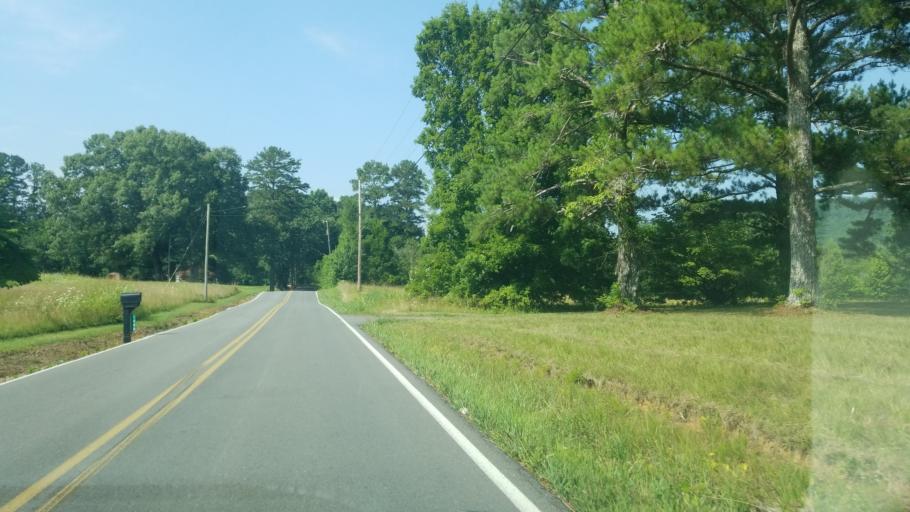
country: US
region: Tennessee
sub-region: Hamilton County
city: Collegedale
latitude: 35.0796
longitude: -84.9966
